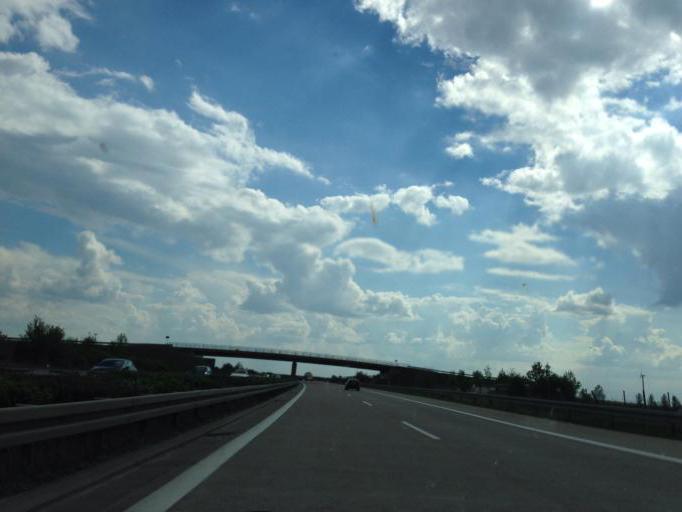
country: DE
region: Saxony-Anhalt
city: Glothe
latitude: 51.8857
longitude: 11.6861
